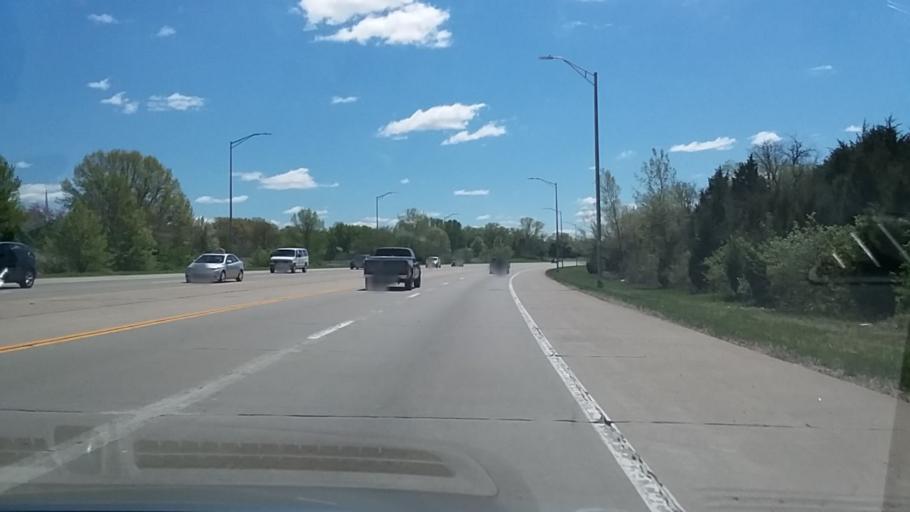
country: US
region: Kansas
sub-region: Johnson County
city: Olathe
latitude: 38.8947
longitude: -94.8365
